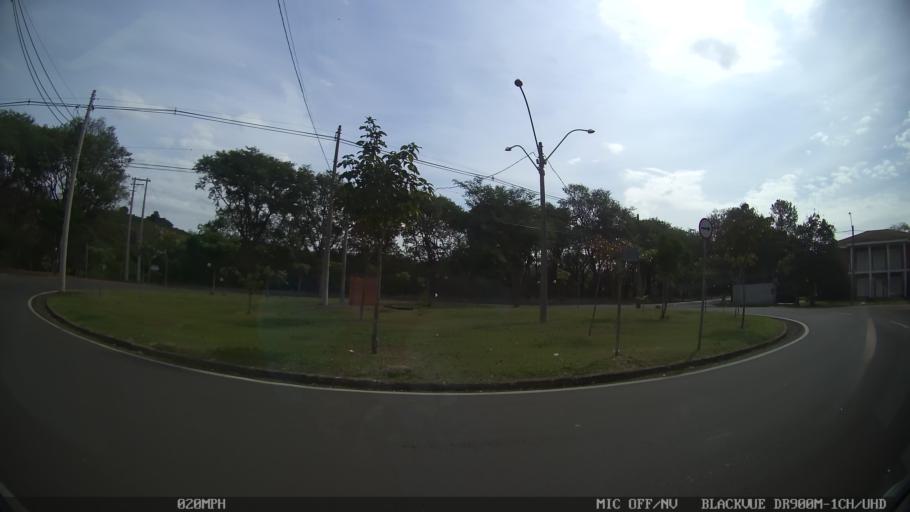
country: BR
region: Sao Paulo
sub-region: Piracicaba
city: Piracicaba
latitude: -22.7117
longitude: -47.6758
